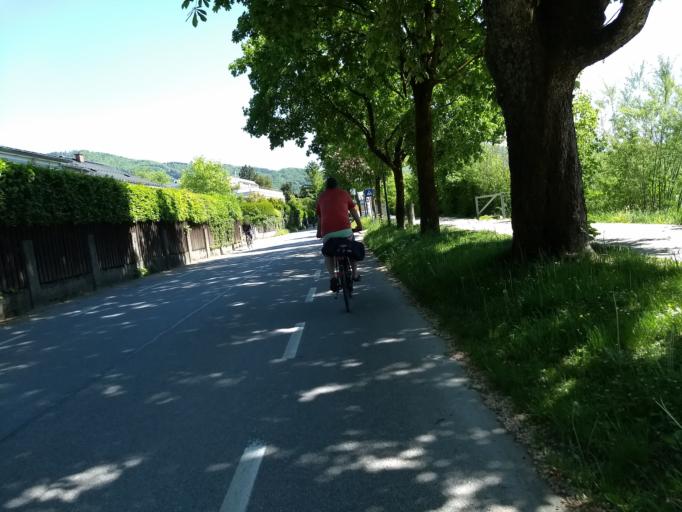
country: AT
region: Salzburg
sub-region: Salzburg Stadt
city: Salzburg
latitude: 47.7919
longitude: 13.0672
